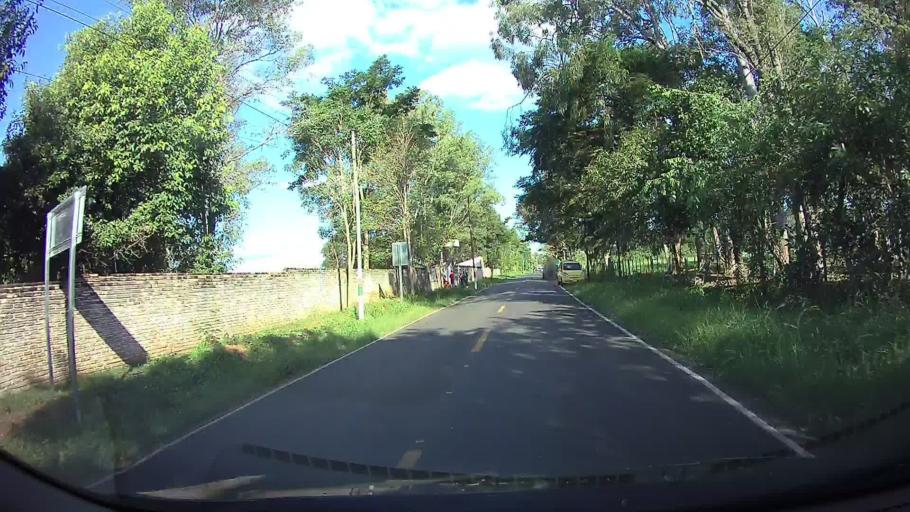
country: PY
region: Central
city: Aregua
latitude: -25.2993
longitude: -57.3904
